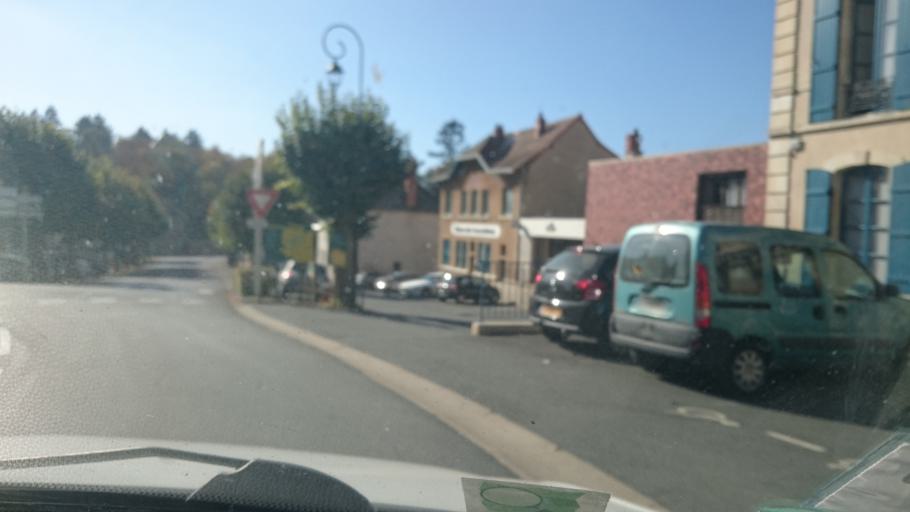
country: FR
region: Auvergne
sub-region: Departement de l'Allier
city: Vallon-en-Sully
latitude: 46.5095
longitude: 2.7116
